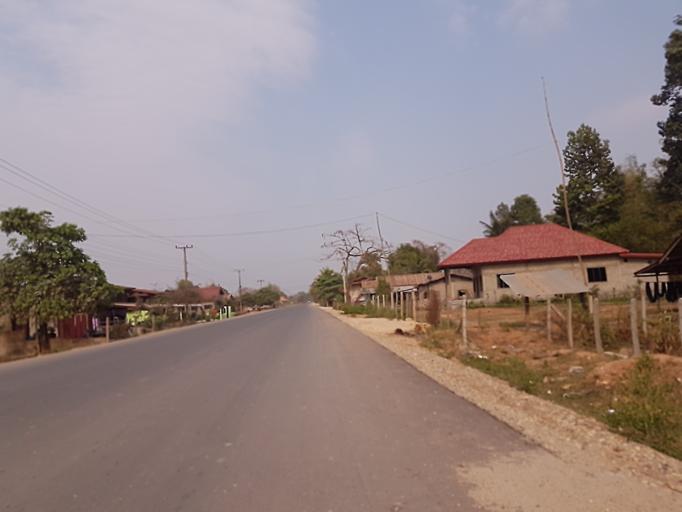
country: TH
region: Nong Khai
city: Nong Khai
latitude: 17.9577
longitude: 102.8303
